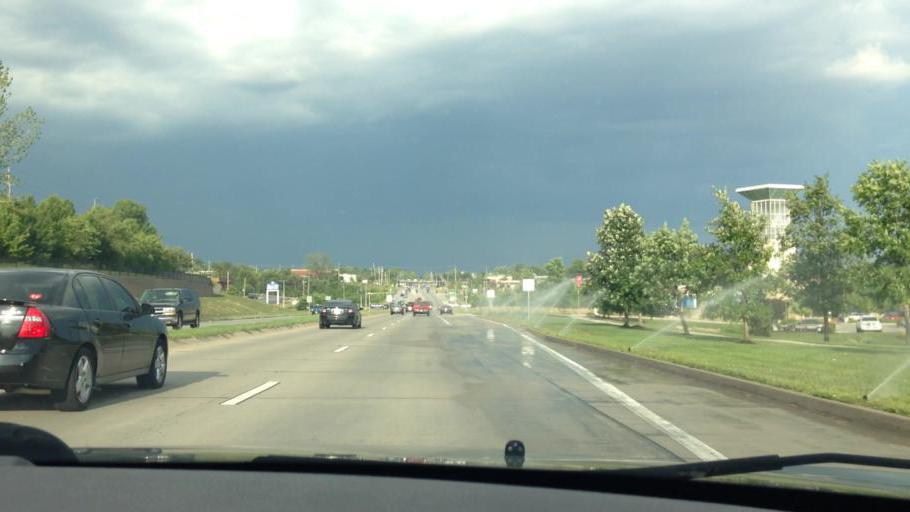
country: US
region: Missouri
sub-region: Platte County
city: Parkville
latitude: 39.2102
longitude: -94.6510
